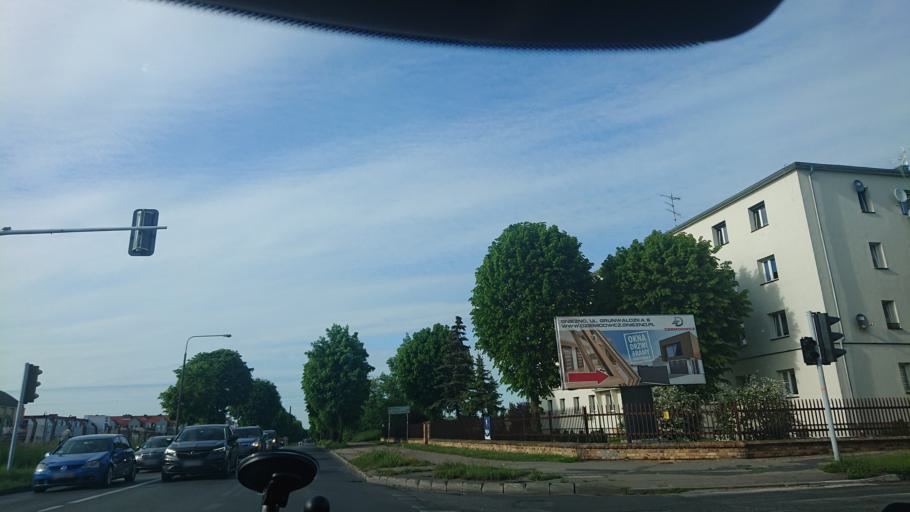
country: PL
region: Greater Poland Voivodeship
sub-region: Powiat gnieznienski
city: Gniezno
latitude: 52.5186
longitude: 17.5958
